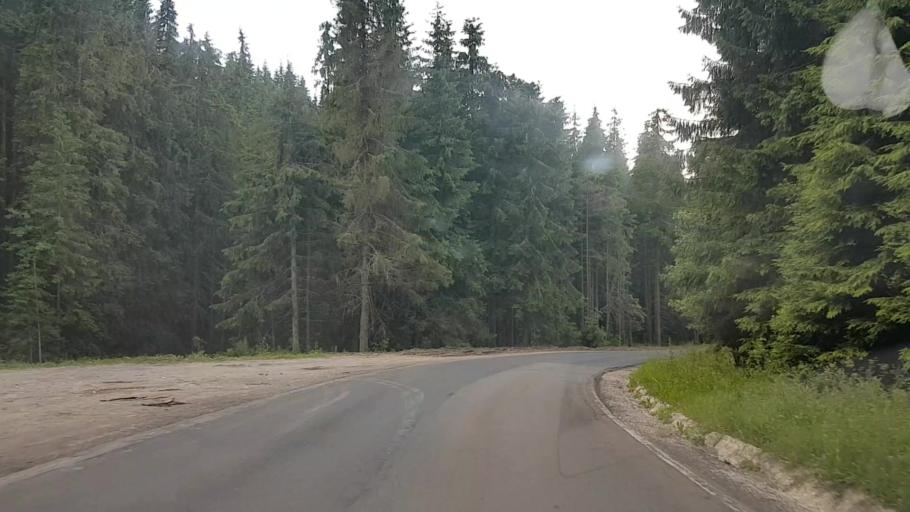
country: RO
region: Harghita
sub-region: Comuna Varsag
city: Varsag
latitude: 46.6426
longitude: 25.2841
